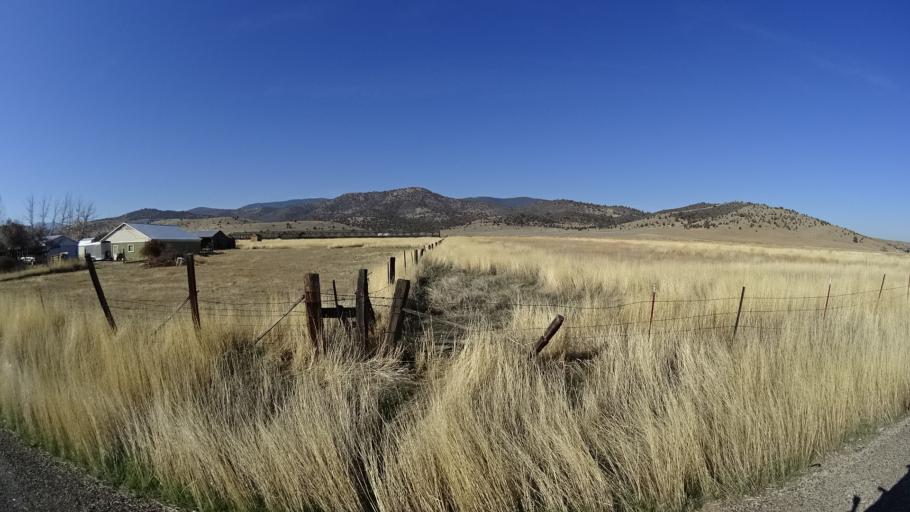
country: US
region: California
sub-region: Siskiyou County
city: Montague
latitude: 41.6192
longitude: -122.5298
